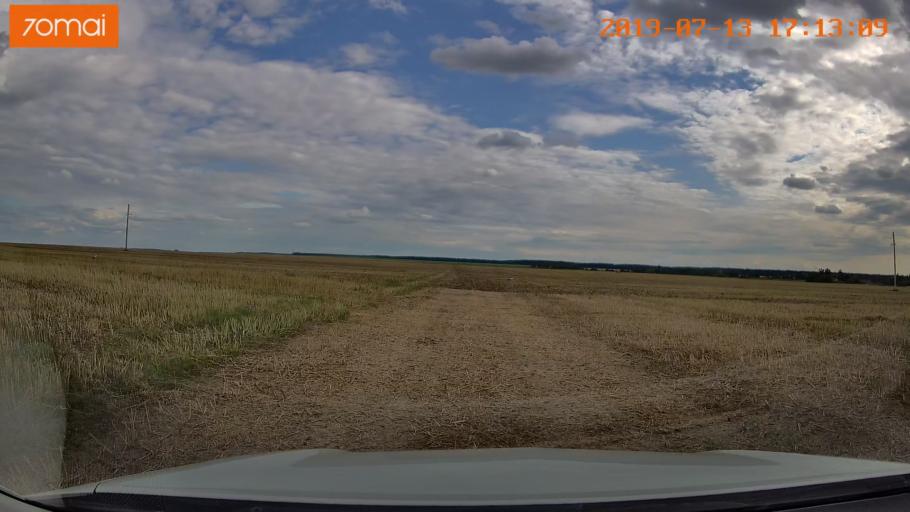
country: BY
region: Mogilev
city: Babruysk
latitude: 53.2674
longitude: 29.2971
